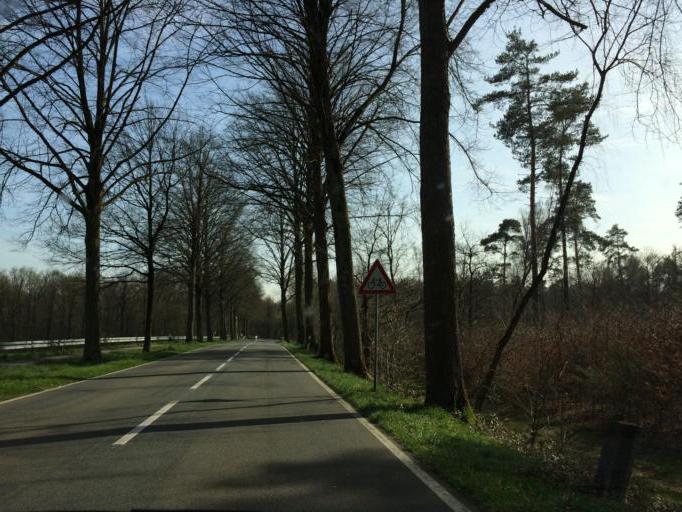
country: DE
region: North Rhine-Westphalia
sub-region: Regierungsbezirk Munster
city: Klein Reken
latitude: 51.7500
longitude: 7.1067
